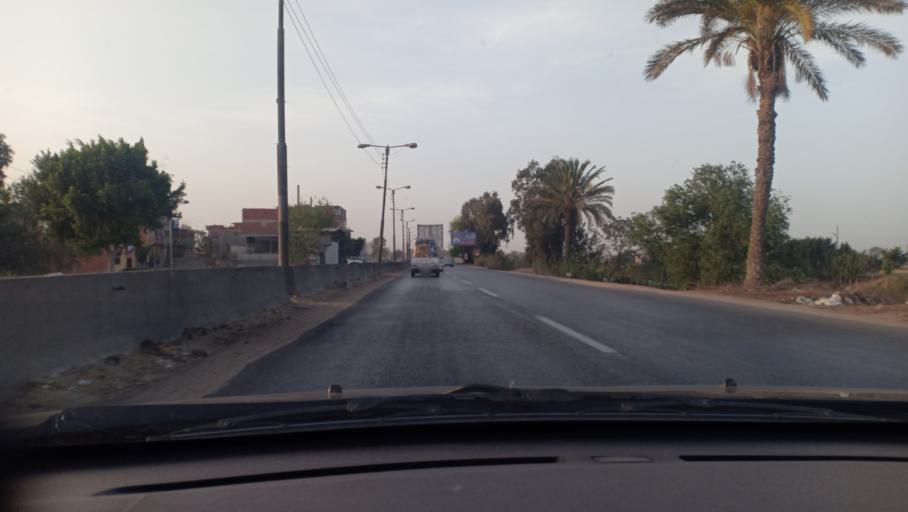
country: EG
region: Muhafazat al Gharbiyah
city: Zifta
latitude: 30.6245
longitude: 31.2790
